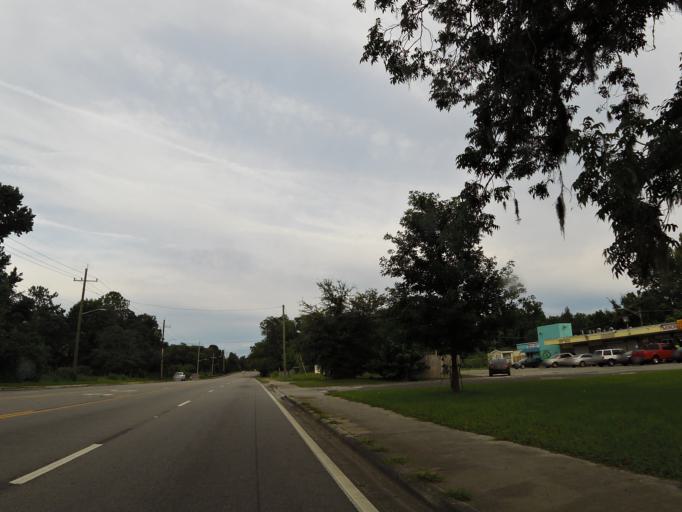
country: US
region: Florida
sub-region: Duval County
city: Jacksonville
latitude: 30.3896
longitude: -81.7241
